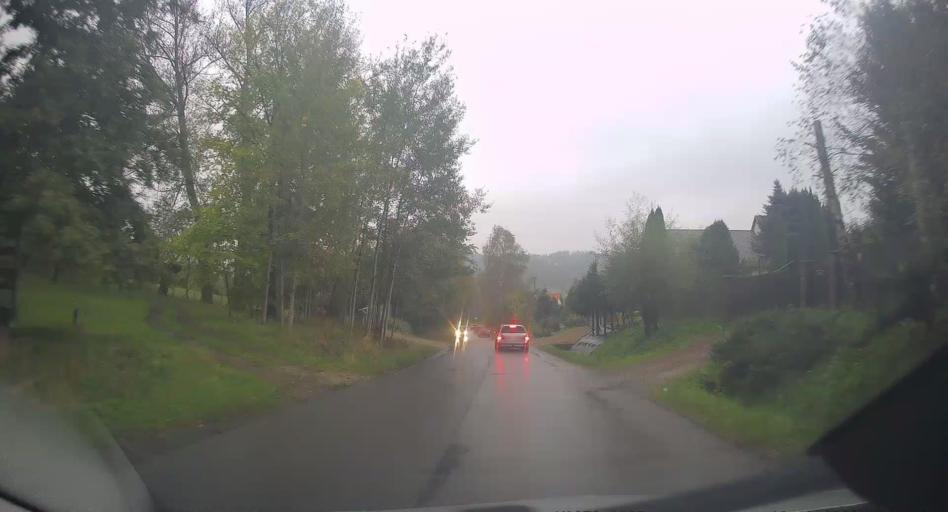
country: PL
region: Lesser Poland Voivodeship
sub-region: Powiat krakowski
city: Ochojno
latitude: 49.9684
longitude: 19.9982
